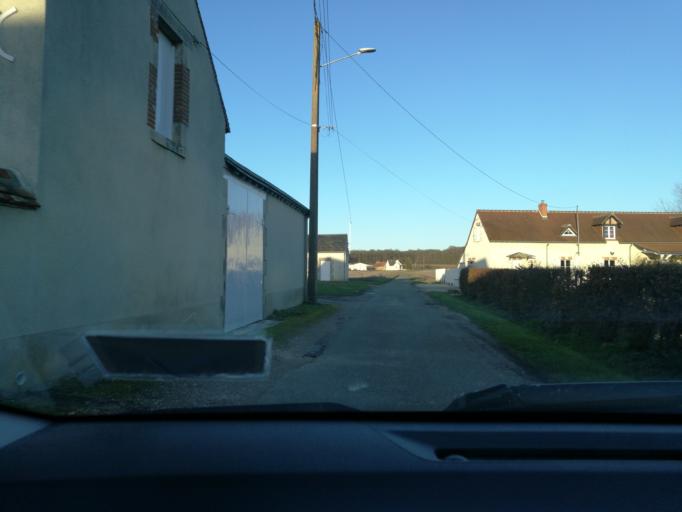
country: FR
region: Centre
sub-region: Departement du Loiret
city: Semoy
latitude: 47.9361
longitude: 1.9608
